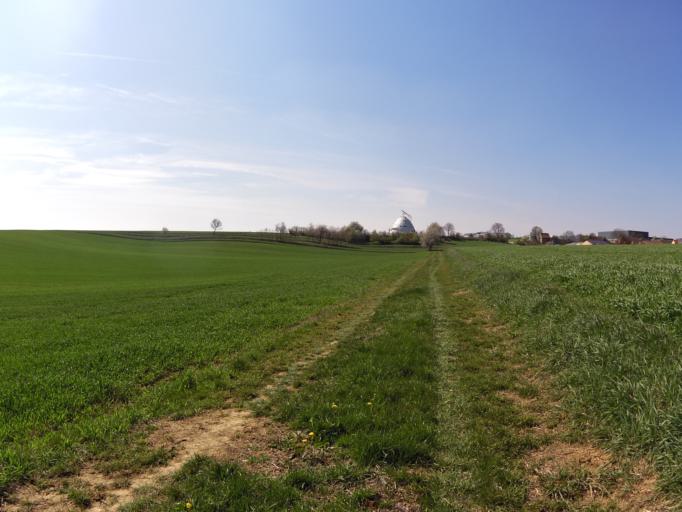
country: DE
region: Bavaria
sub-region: Regierungsbezirk Unterfranken
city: Biebelried
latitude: 49.7796
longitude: 10.0798
